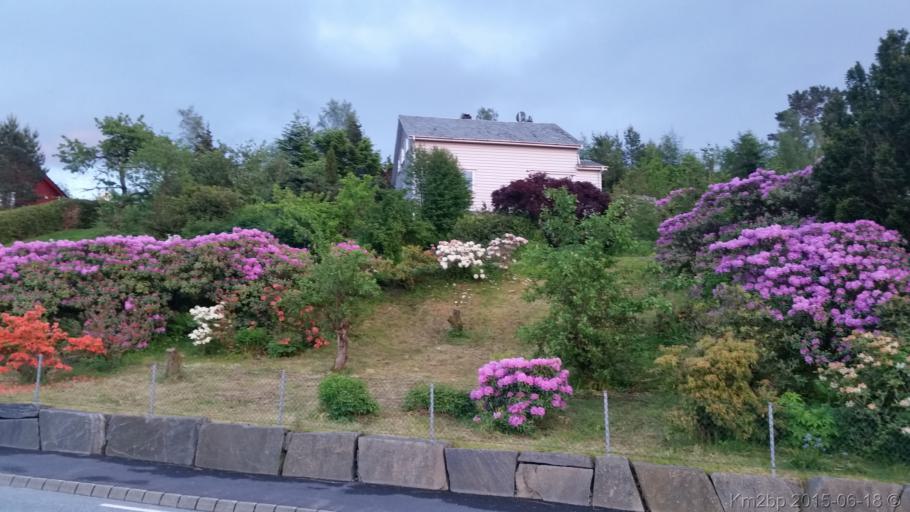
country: NO
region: Rogaland
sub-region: Hjelmeland
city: Hjelmelandsvagen
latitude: 59.2328
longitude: 6.1667
